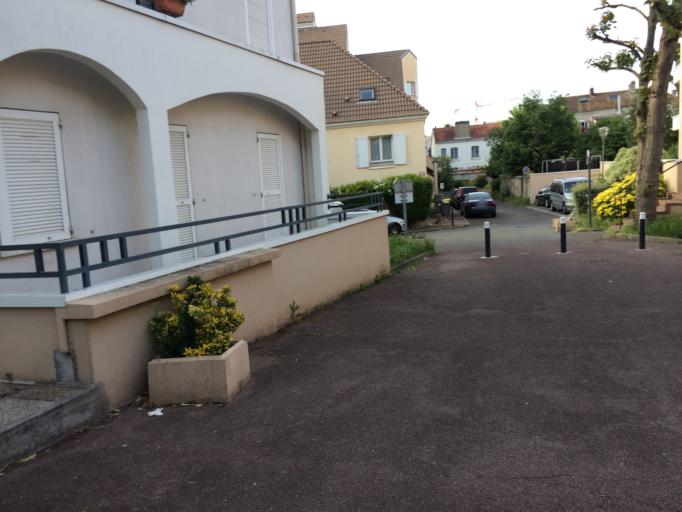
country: FR
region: Ile-de-France
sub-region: Departement de l'Essonne
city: Longjumeau
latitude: 48.6964
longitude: 2.2940
